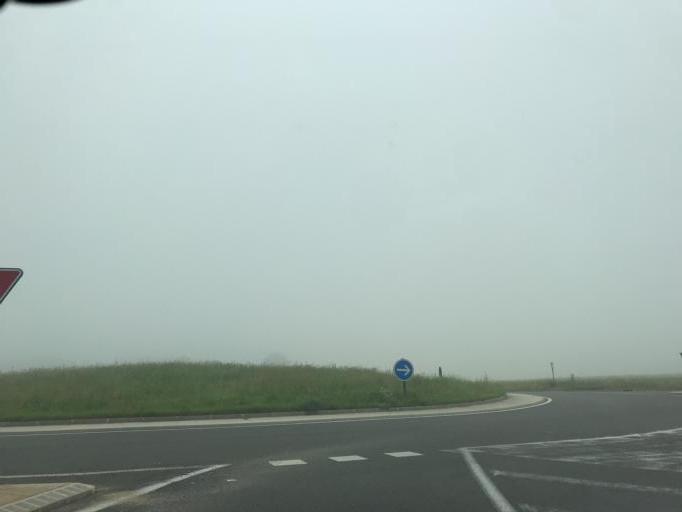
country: FR
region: Ile-de-France
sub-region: Departement de Seine-et-Marne
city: Coupvray
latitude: 48.8832
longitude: 2.8059
